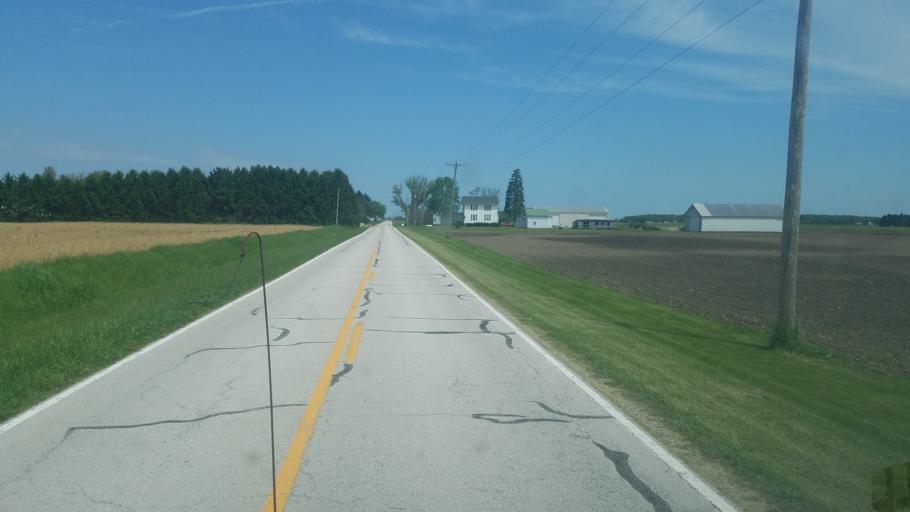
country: US
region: Ohio
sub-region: Ottawa County
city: Oak Harbor
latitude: 41.4443
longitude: -83.2016
